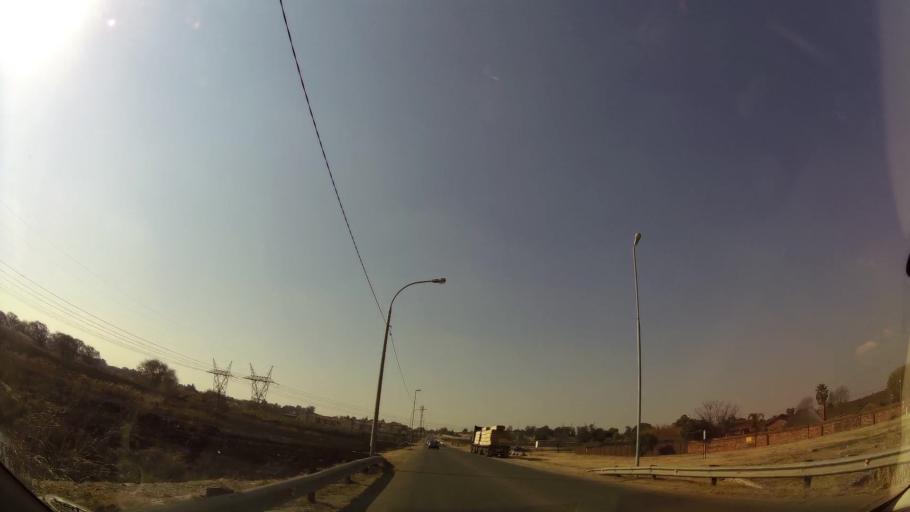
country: ZA
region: Gauteng
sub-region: Ekurhuleni Metropolitan Municipality
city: Benoni
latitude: -26.1417
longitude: 28.2848
